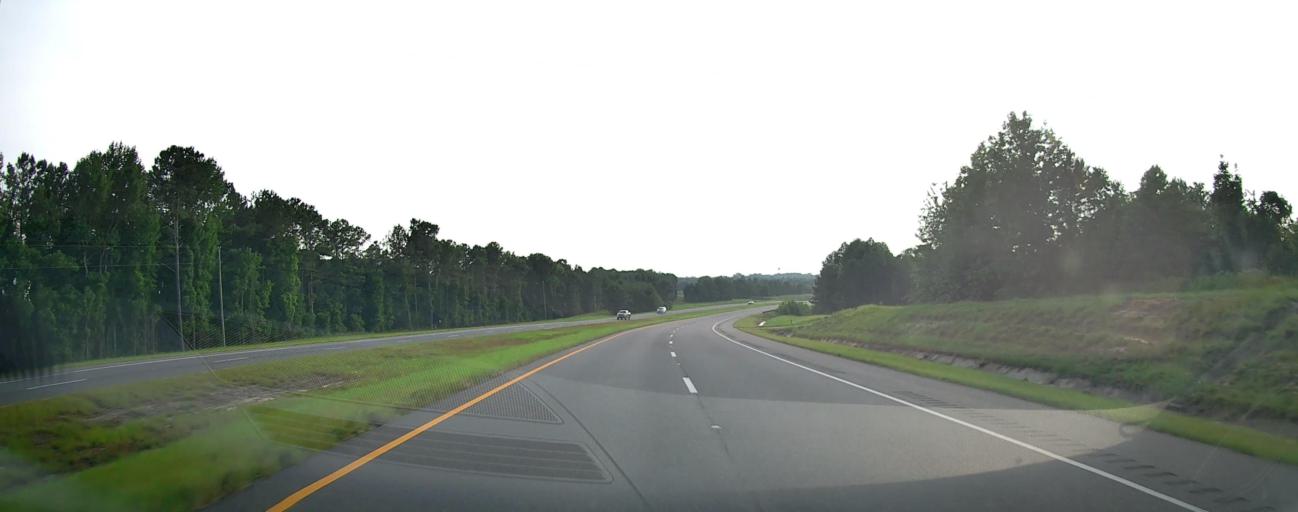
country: US
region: Georgia
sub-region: Talbot County
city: Talbotton
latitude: 32.5791
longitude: -84.5273
